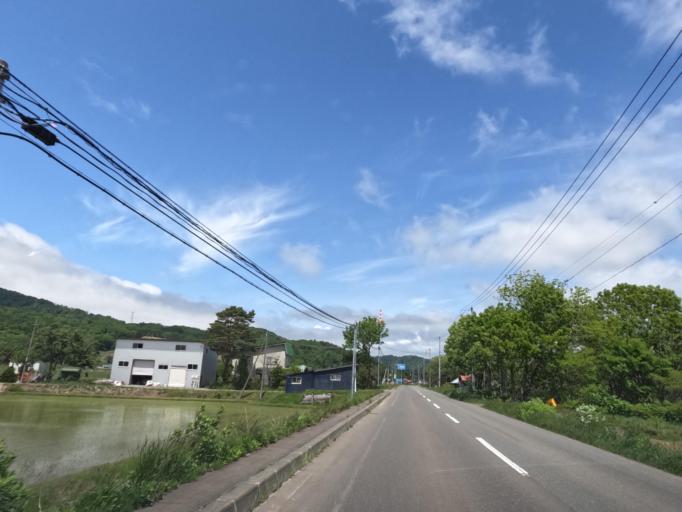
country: JP
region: Hokkaido
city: Tobetsu
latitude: 43.2905
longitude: 141.5386
